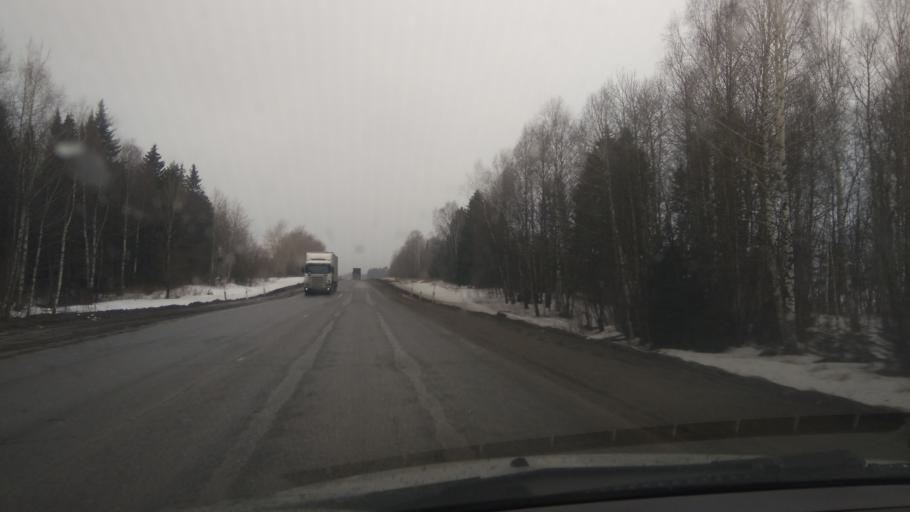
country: RU
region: Perm
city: Kukushtan
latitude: 57.6190
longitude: 56.4855
